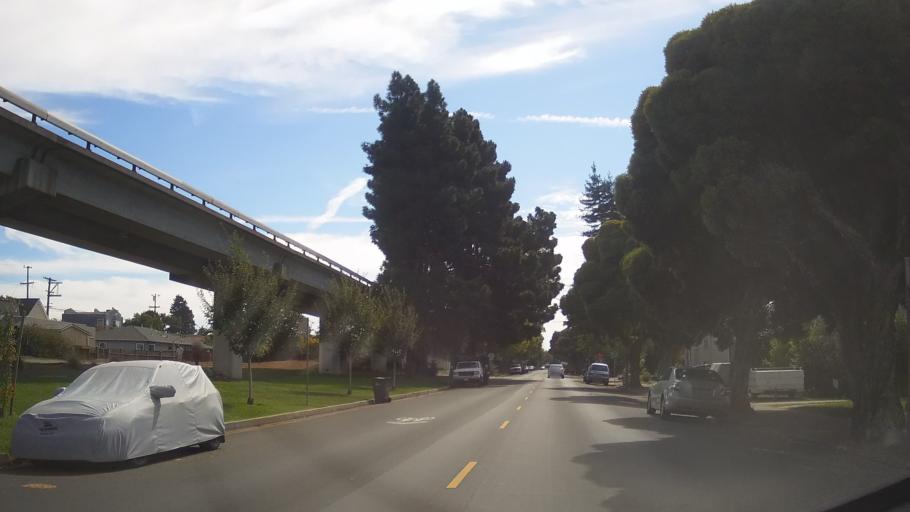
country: US
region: California
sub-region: Alameda County
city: Albany
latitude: 37.8858
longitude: -122.2921
